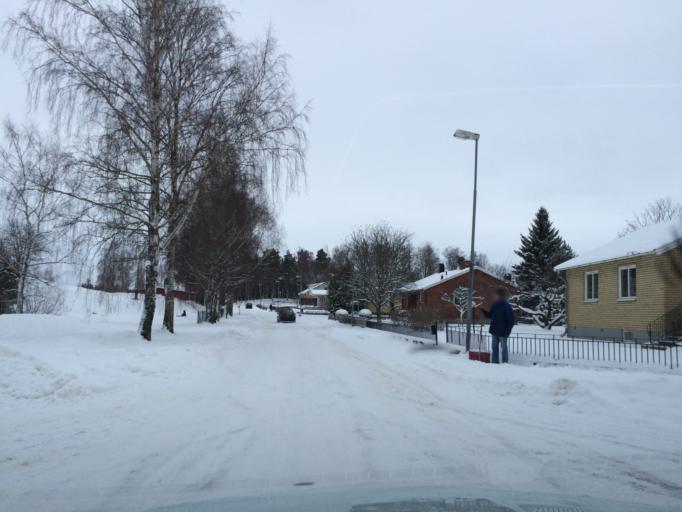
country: SE
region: Vaestmanland
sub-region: Hallstahammars Kommun
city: Hallstahammar
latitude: 59.6199
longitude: 16.2422
